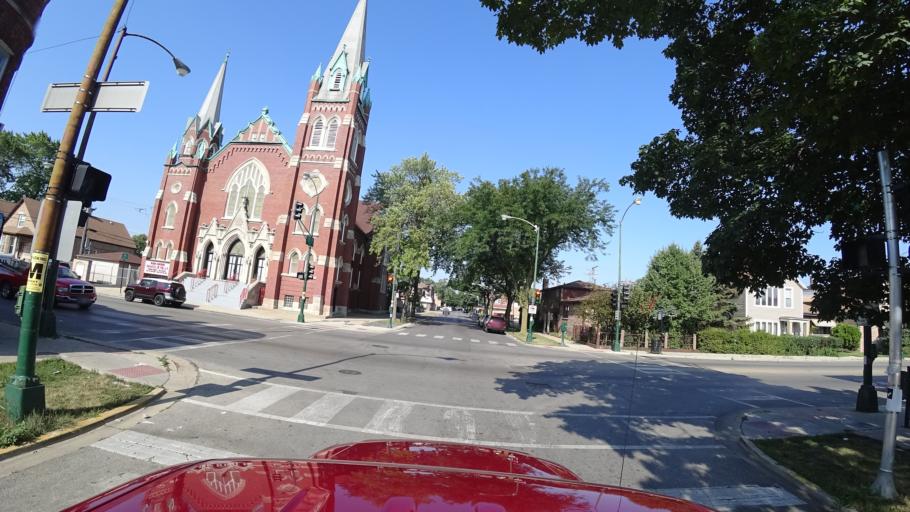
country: US
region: Illinois
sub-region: Cook County
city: Chicago
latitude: 41.8156
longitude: -87.6942
